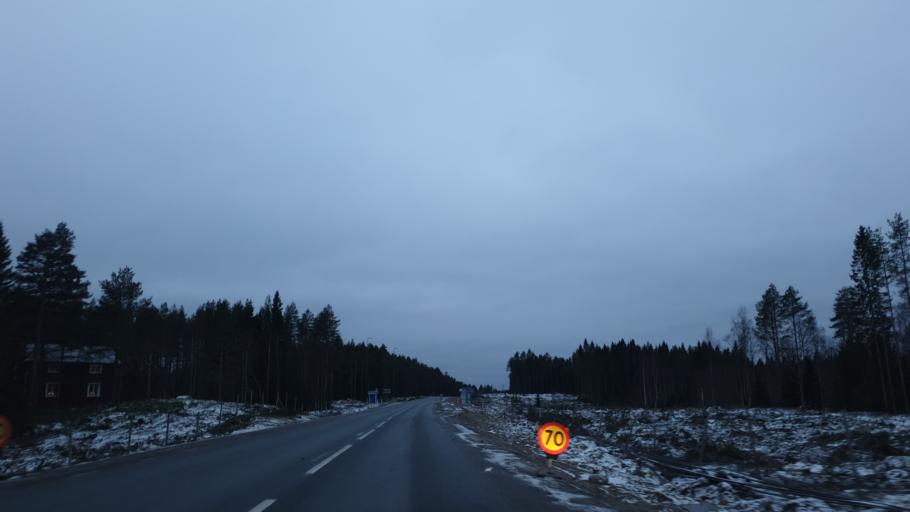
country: SE
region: Vaesterbotten
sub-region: Robertsfors Kommun
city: Robertsfors
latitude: 64.0008
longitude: 20.7927
